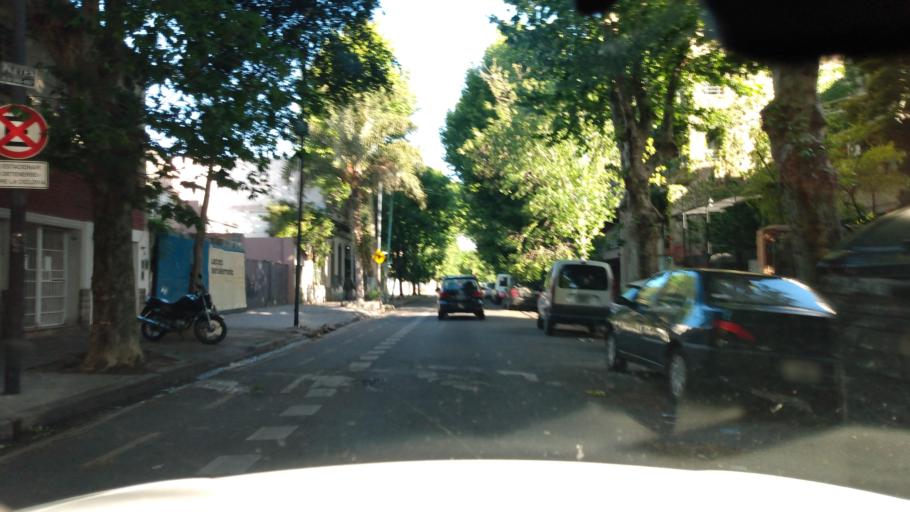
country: AR
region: Buenos Aires F.D.
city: Villa Santa Rita
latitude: -34.5815
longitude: -58.4905
